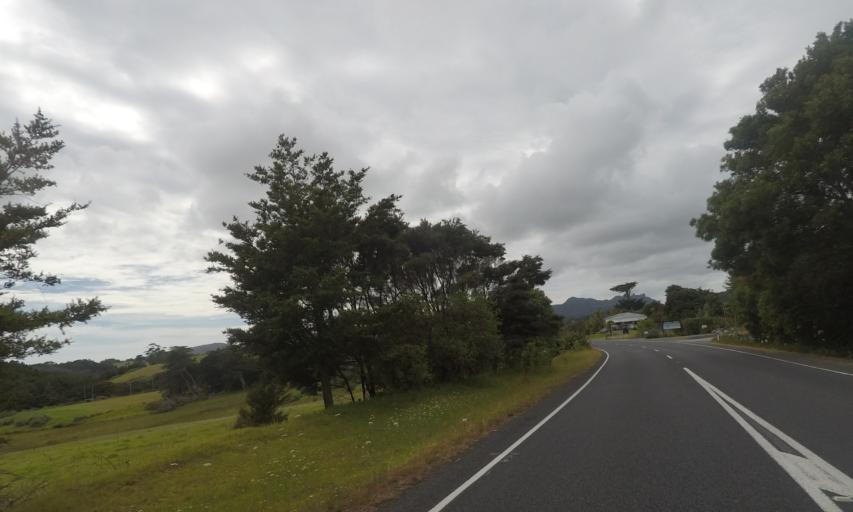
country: NZ
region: Northland
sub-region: Whangarei
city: Ruakaka
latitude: -35.7668
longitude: 174.4755
